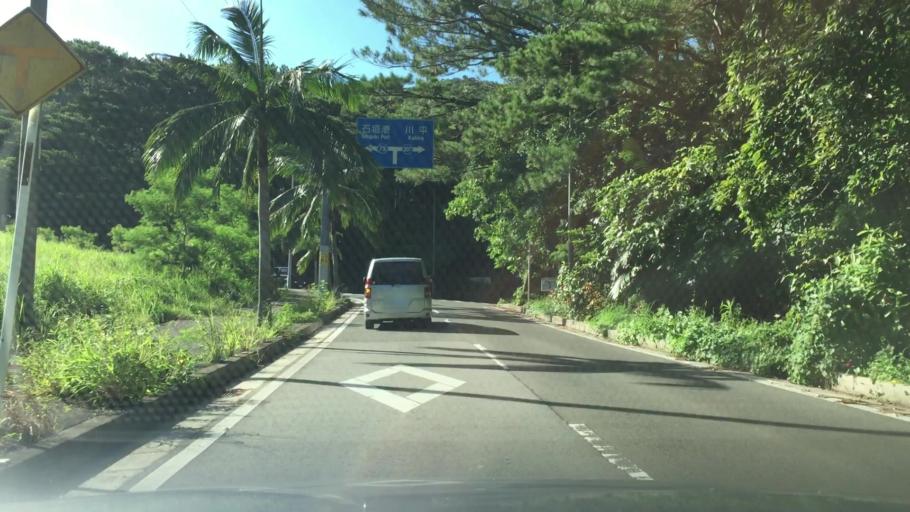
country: JP
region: Okinawa
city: Ishigaki
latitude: 24.4483
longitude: 124.1330
